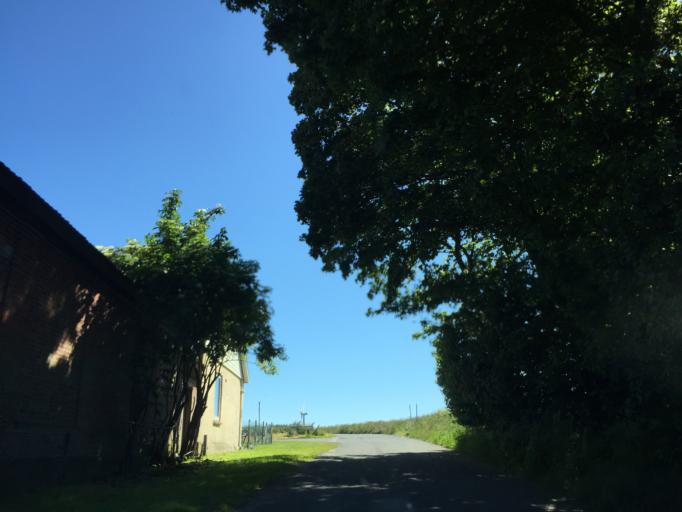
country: DK
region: Central Jutland
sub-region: Viborg Kommune
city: Bjerringbro
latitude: 56.2614
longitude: 9.6901
